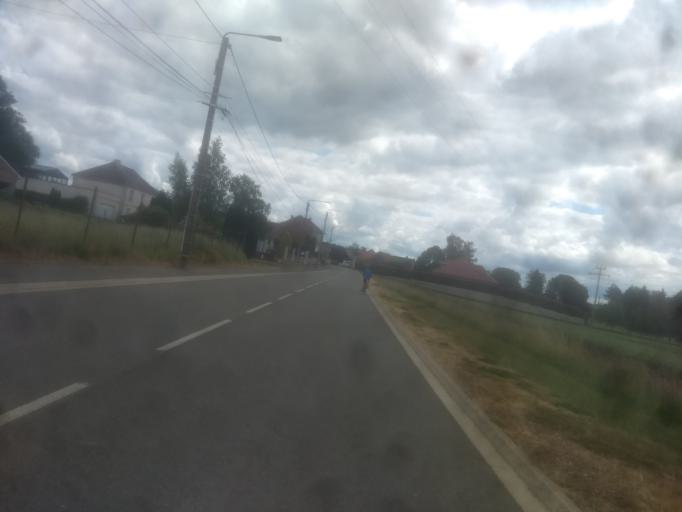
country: FR
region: Nord-Pas-de-Calais
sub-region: Departement du Pas-de-Calais
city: Agny
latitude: 50.2131
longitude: 2.7763
